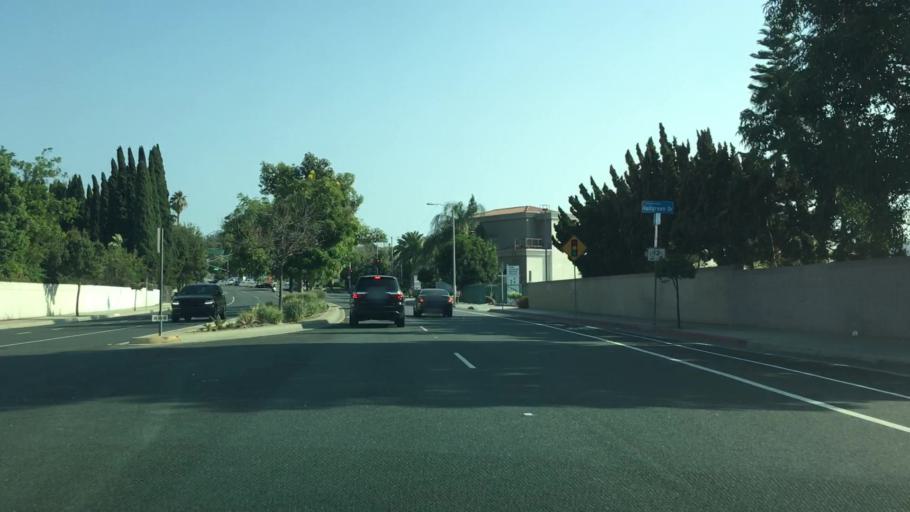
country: US
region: California
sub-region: Los Angeles County
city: Walnut
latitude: 33.9893
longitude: -117.8702
